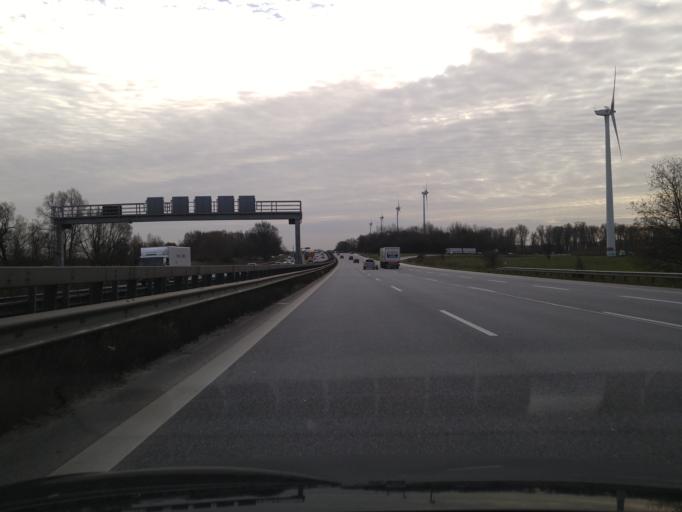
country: DE
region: Hamburg
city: Harburg
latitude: 53.4679
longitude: 10.0243
